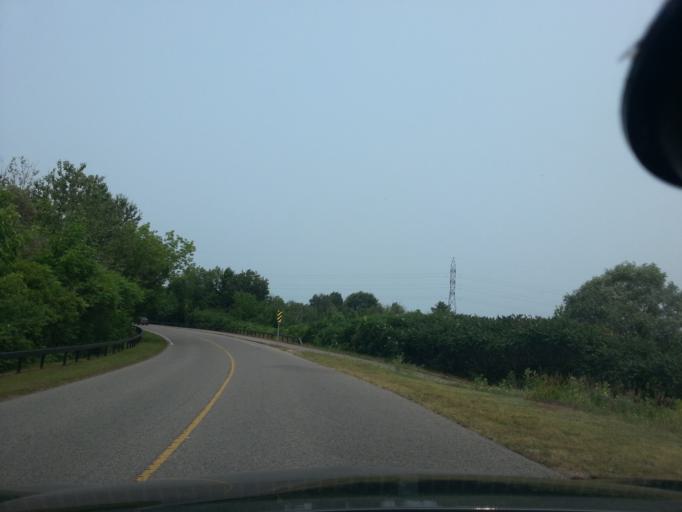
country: CA
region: Quebec
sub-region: Outaouais
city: Gatineau
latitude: 45.4443
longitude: -75.7604
